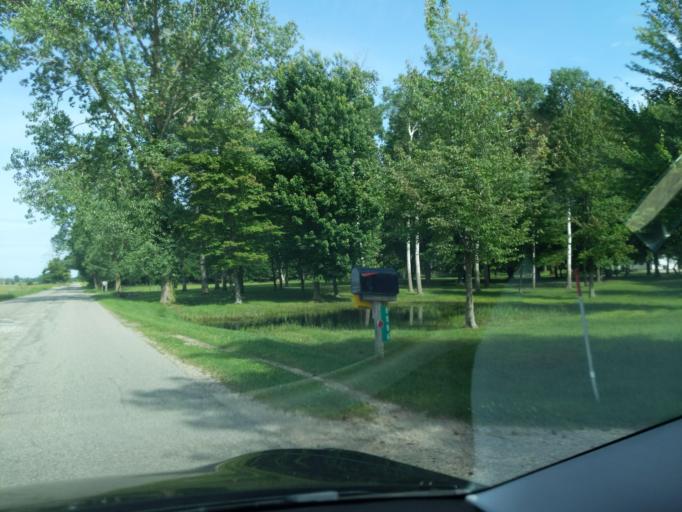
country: US
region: Michigan
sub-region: Newaygo County
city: Fremont
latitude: 43.4205
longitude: -86.0215
